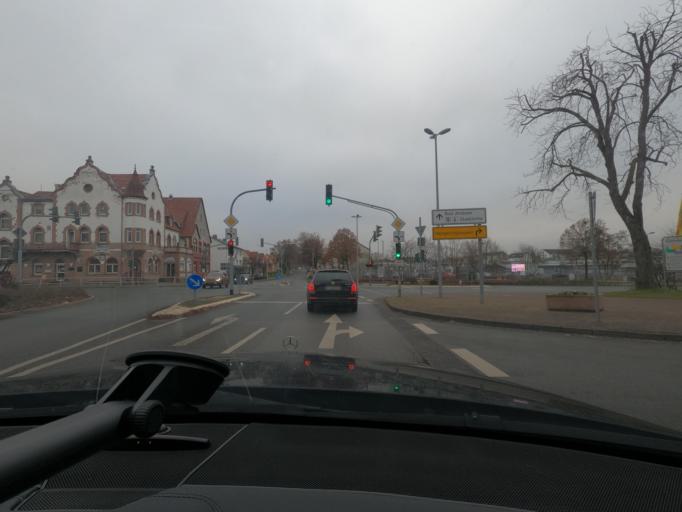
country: DE
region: Hesse
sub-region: Regierungsbezirk Kassel
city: Bad Arolsen
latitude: 51.3819
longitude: 8.9986
